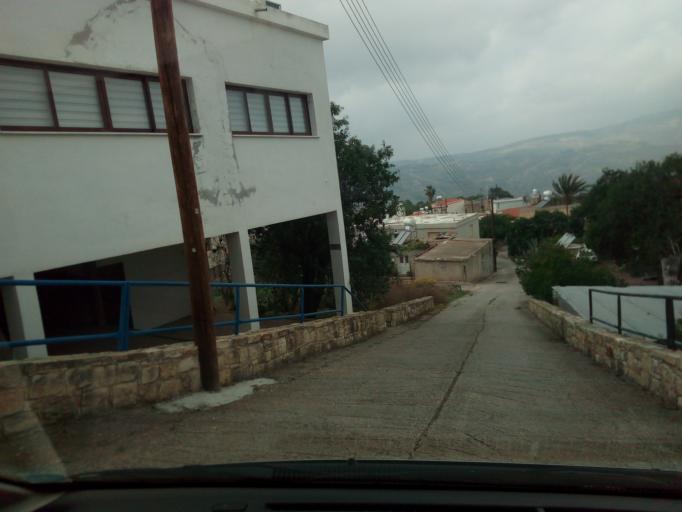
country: CY
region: Limassol
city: Pachna
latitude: 34.8118
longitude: 32.6510
